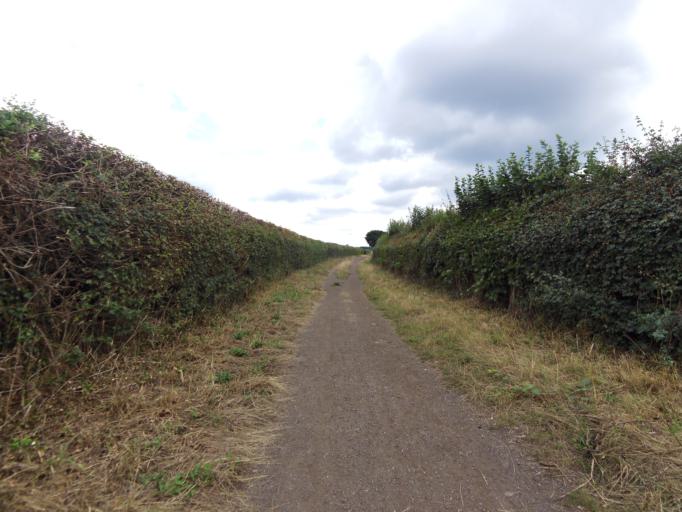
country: GB
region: England
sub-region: Hertfordshire
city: Shenley AV
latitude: 51.7048
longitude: -0.2854
